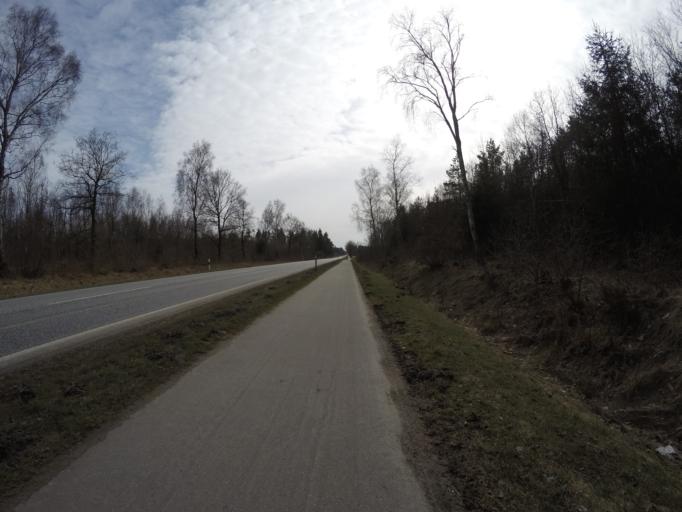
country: DE
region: Schleswig-Holstein
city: Lentfohrden
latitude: 53.8417
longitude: 9.8858
